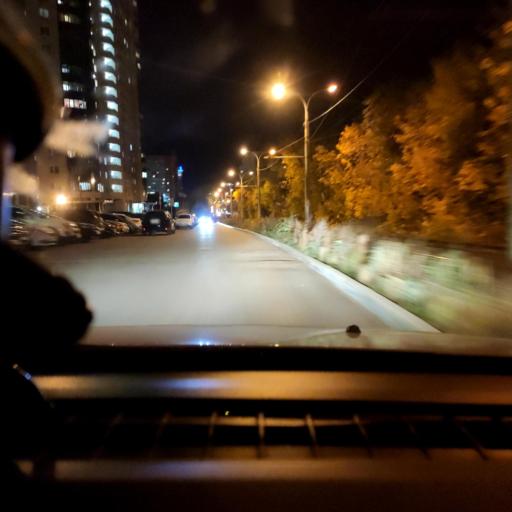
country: RU
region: Samara
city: Samara
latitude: 53.2191
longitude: 50.1700
